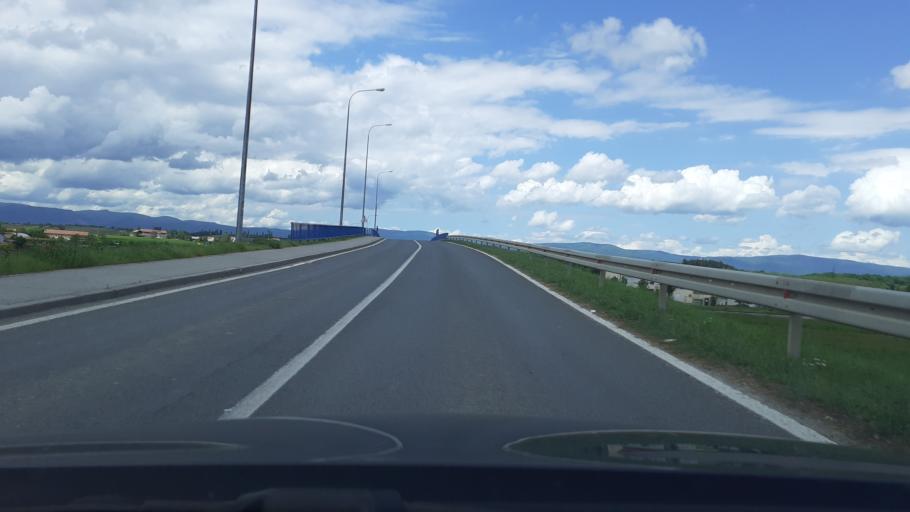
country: HR
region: Pozesko-Slavonska
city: Vidovci
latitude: 45.3344
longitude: 17.7090
